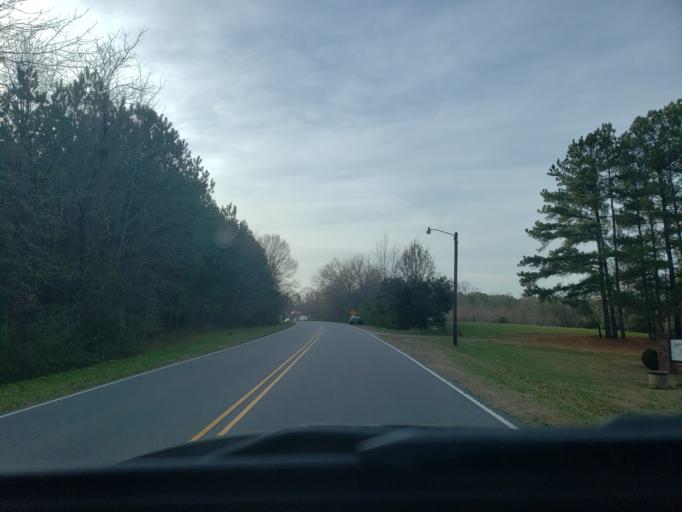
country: US
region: North Carolina
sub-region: Cleveland County
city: Boiling Springs
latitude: 35.3046
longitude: -81.7043
